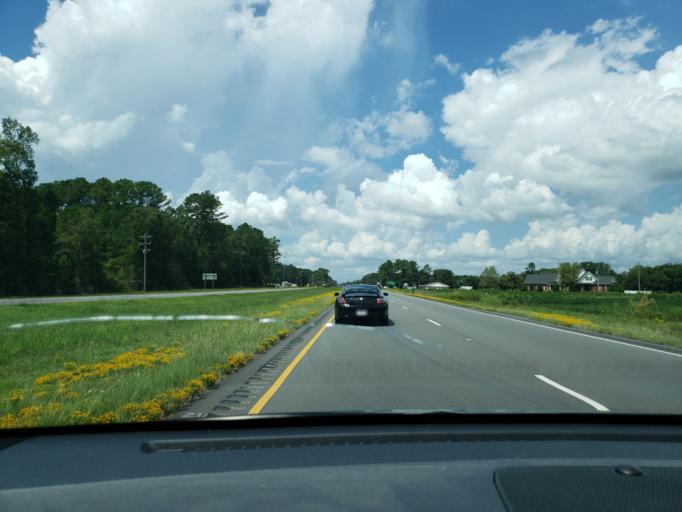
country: US
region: North Carolina
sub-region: Robeson County
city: Saint Pauls
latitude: 34.7912
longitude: -78.8158
